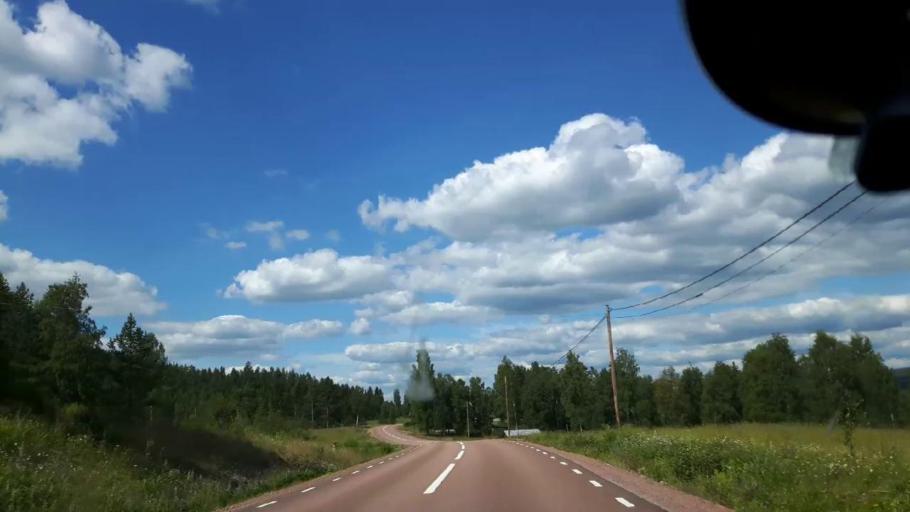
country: SE
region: Jaemtland
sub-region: Ragunda Kommun
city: Hammarstrand
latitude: 63.0402
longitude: 16.5168
